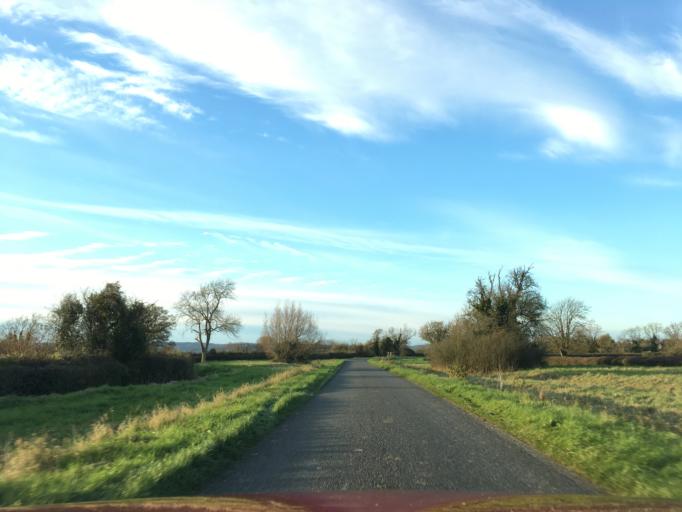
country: GB
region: England
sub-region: South Gloucestershire
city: Hill
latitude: 51.6492
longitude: -2.5162
